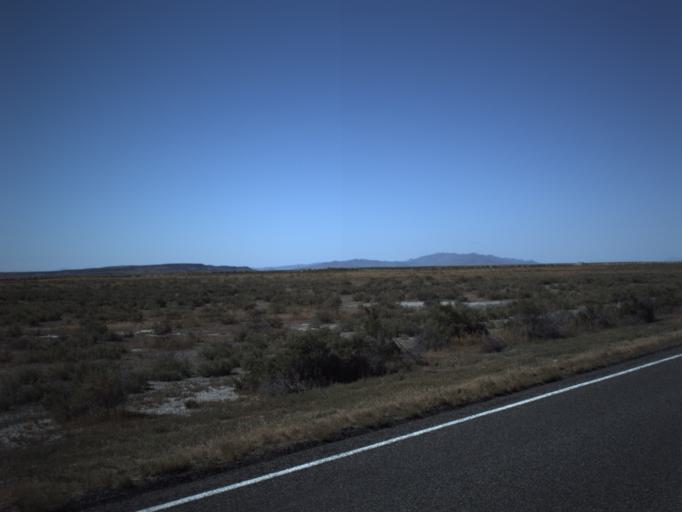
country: US
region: Utah
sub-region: Millard County
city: Delta
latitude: 39.3230
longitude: -112.7359
